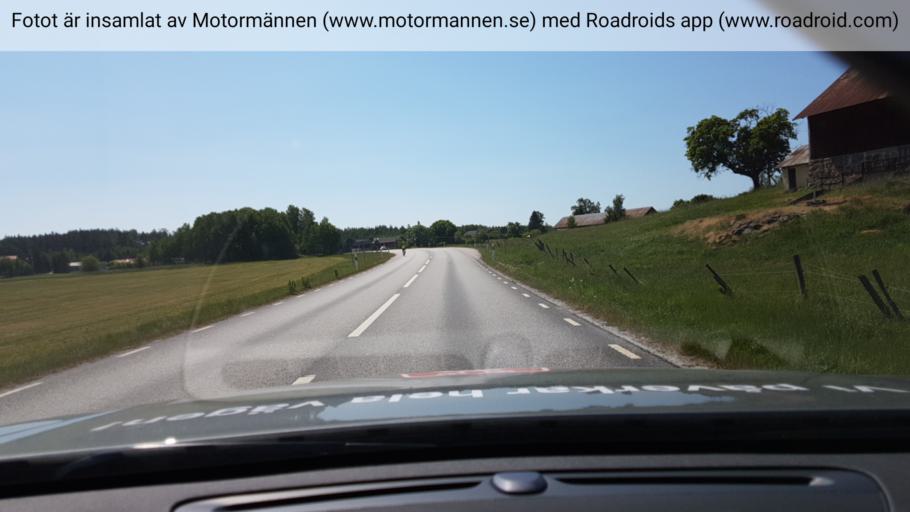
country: SE
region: Stockholm
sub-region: Norrtalje Kommun
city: Rimbo
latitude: 59.6499
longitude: 18.3356
